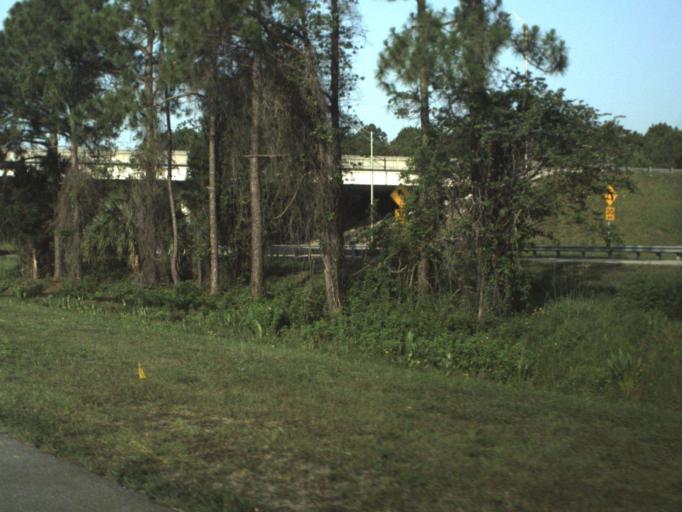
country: US
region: Florida
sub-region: Volusia County
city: Daytona Beach
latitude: 29.1735
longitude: -81.0838
